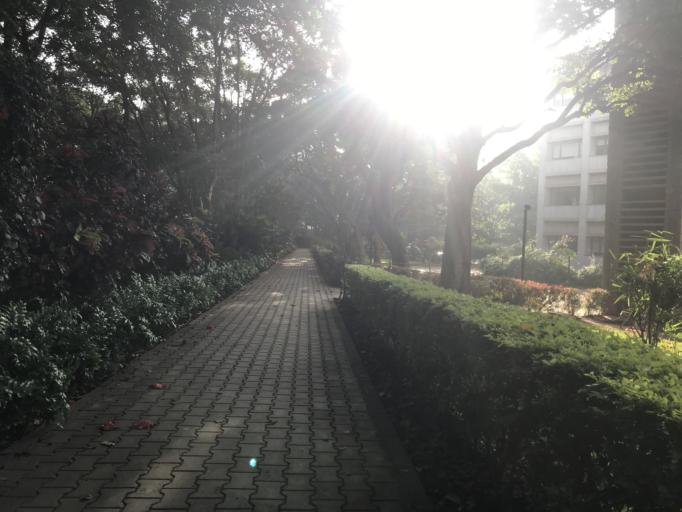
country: IN
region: Karnataka
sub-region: Bangalore Urban
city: Yelahanka
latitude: 13.0721
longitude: 77.5803
